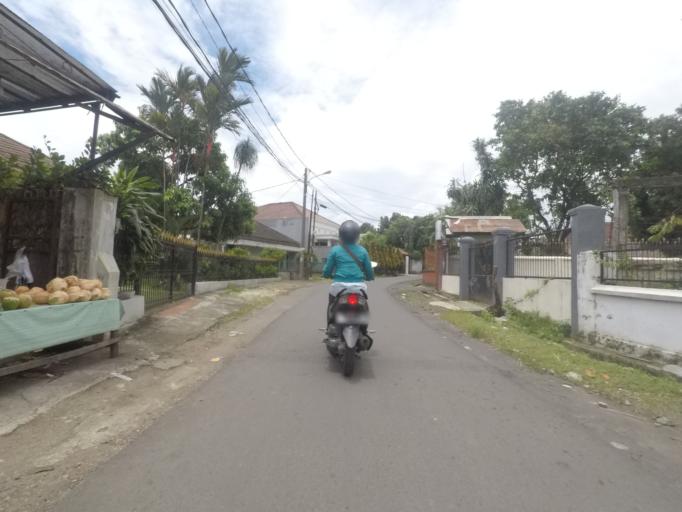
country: ID
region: West Java
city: Bogor
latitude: -6.5896
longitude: 106.7887
